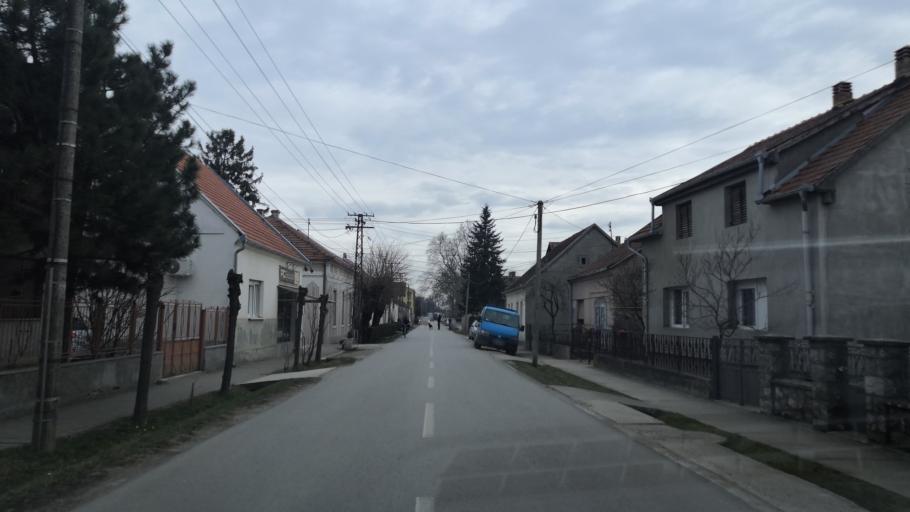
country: RS
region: Autonomna Pokrajina Vojvodina
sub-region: Sremski Okrug
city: Ingija
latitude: 45.0539
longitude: 20.0860
